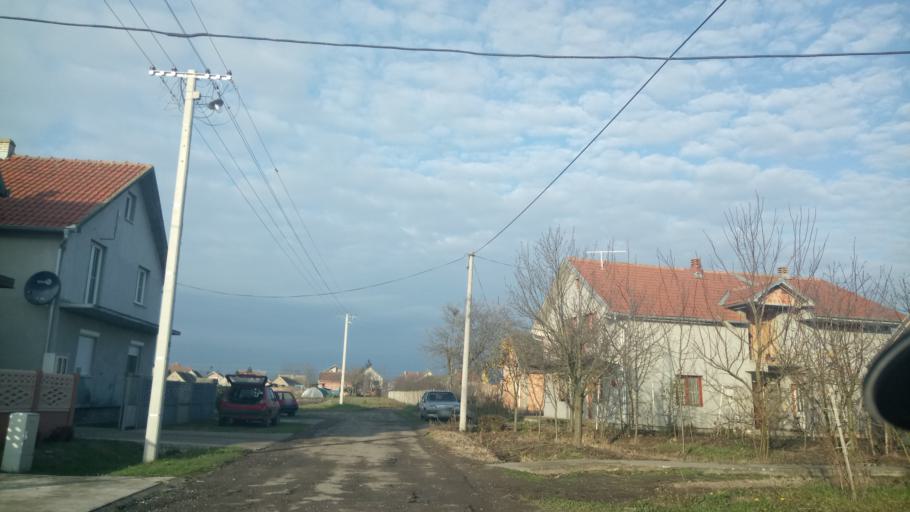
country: RS
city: Vojka
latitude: 44.9333
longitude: 20.1484
